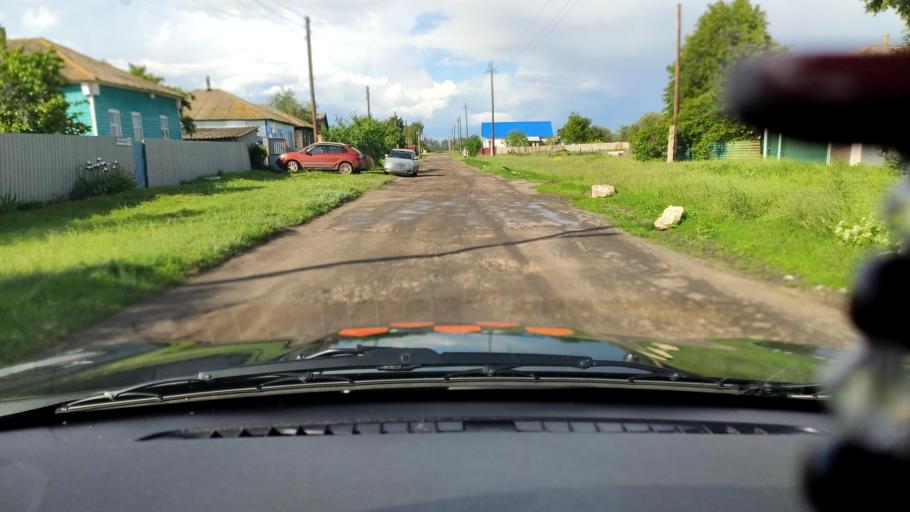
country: RU
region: Voronezj
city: Uryv-Pokrovka
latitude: 51.1185
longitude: 39.1844
